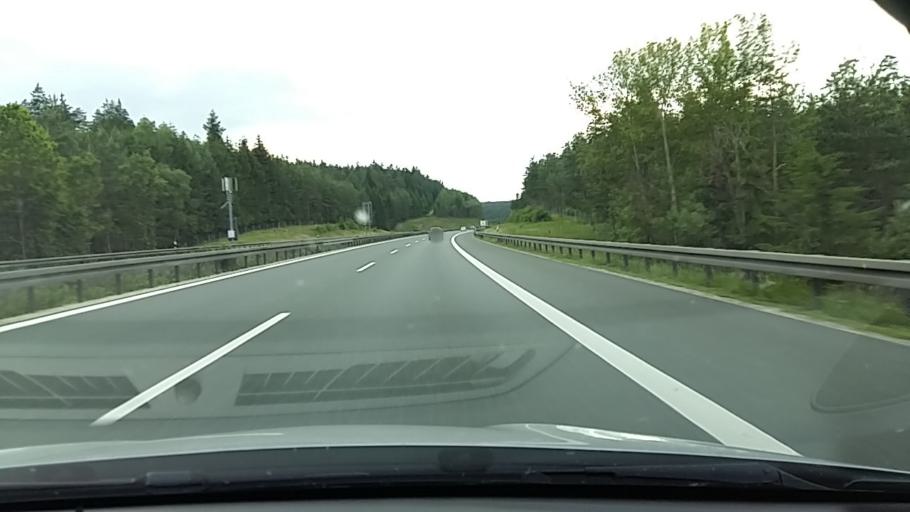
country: DE
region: Bavaria
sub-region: Upper Palatinate
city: Amberg
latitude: 49.3992
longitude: 11.8390
